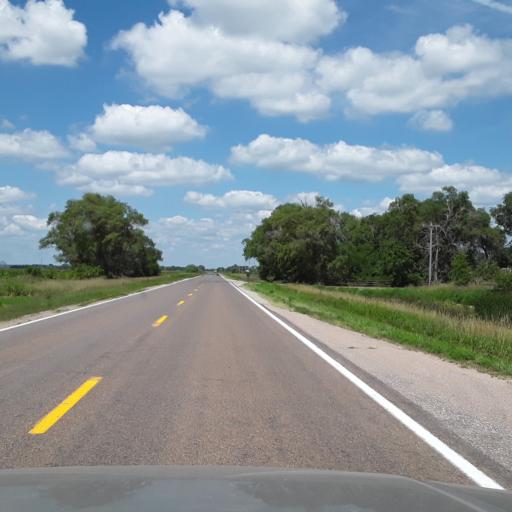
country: US
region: Nebraska
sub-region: Nance County
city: Genoa
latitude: 41.3752
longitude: -97.6944
